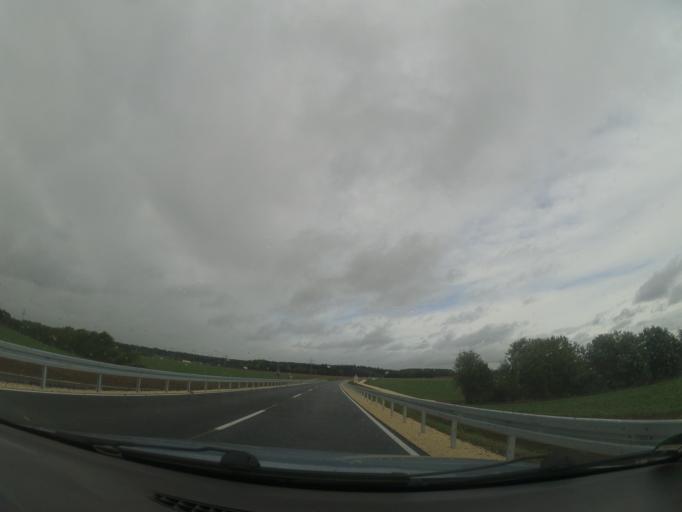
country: DE
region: Baden-Wuerttemberg
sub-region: Tuebingen Region
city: Beimerstetten
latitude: 48.4688
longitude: 9.9694
